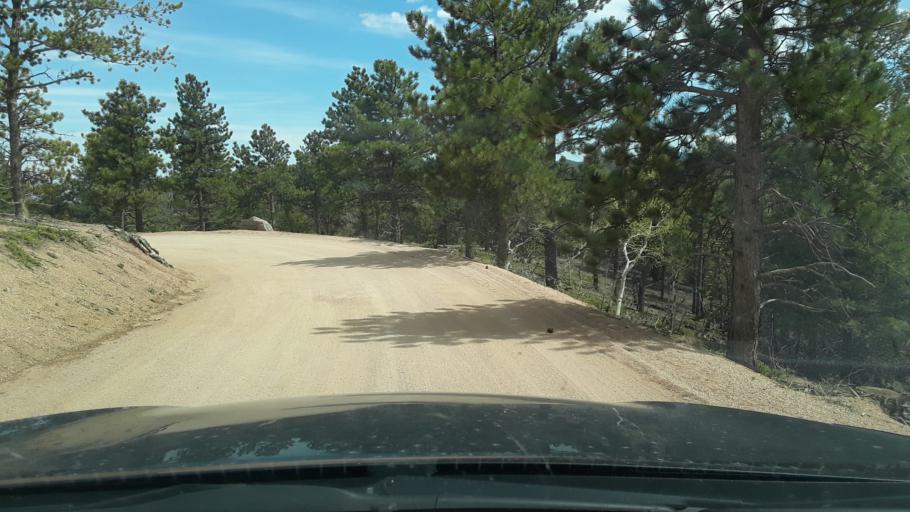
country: US
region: Colorado
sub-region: El Paso County
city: Palmer Lake
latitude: 39.0679
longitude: -104.9466
